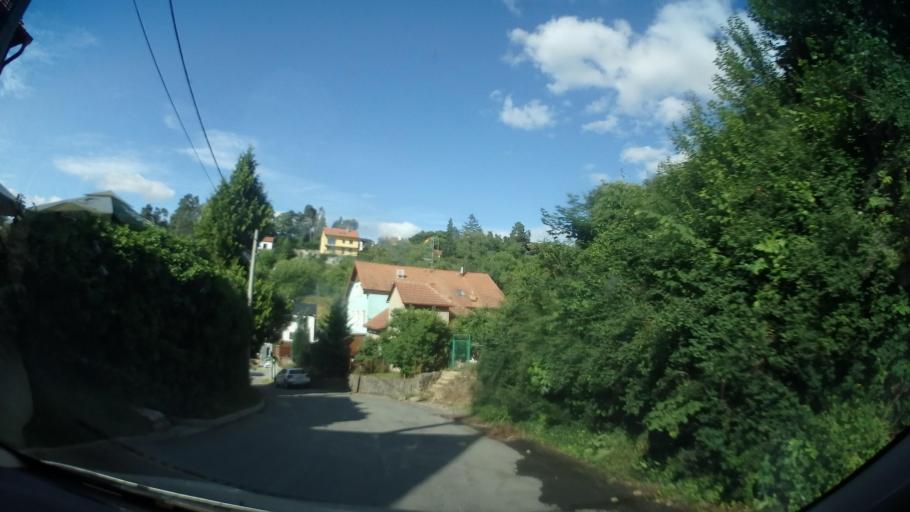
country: CZ
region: South Moravian
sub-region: Okres Brno-Venkov
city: Lelekovice
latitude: 49.3097
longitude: 16.6138
